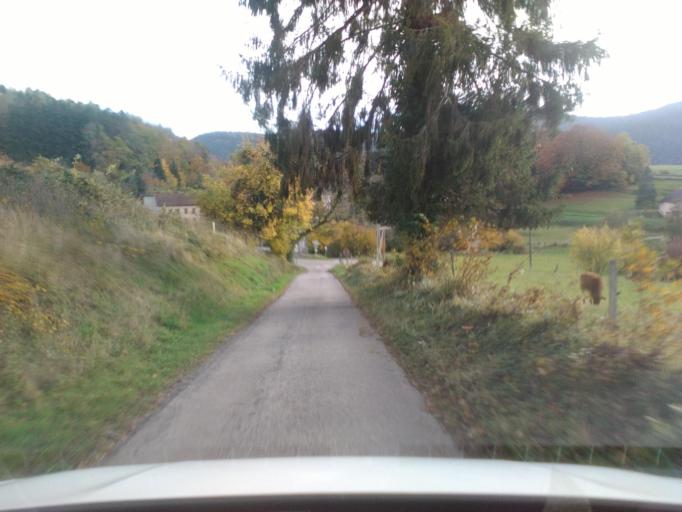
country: FR
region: Lorraine
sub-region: Departement des Vosges
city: Senones
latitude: 48.3354
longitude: 7.0184
